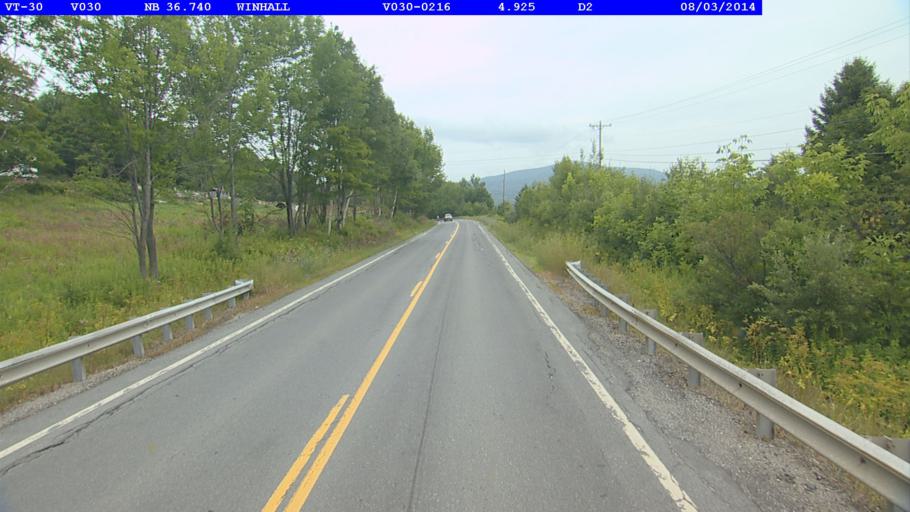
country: US
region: Vermont
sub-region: Bennington County
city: Manchester Center
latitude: 43.1800
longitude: -72.9280
